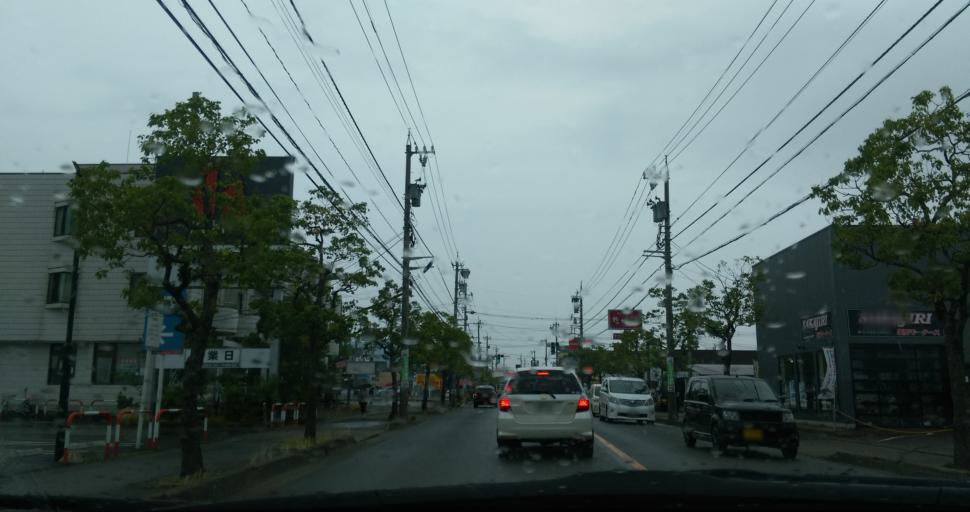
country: JP
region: Fukui
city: Fukui-shi
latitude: 36.0559
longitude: 136.1878
